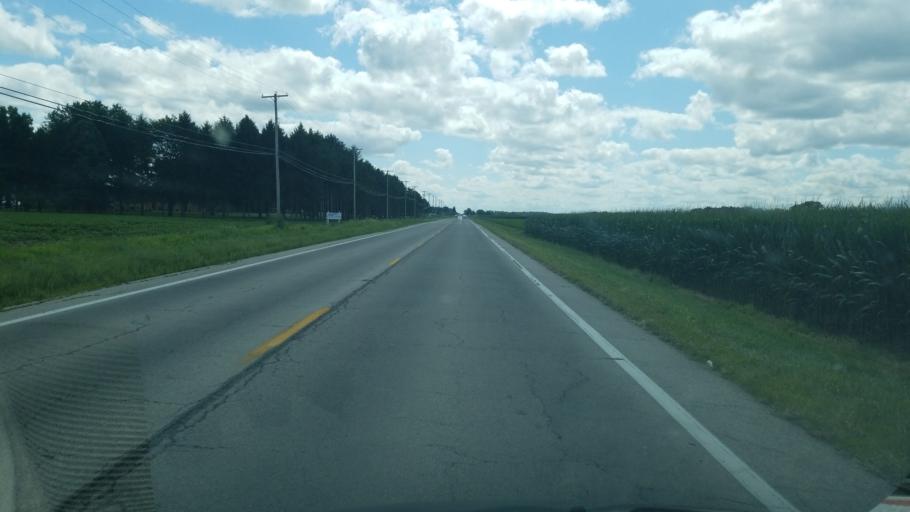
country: US
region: Ohio
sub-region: Henry County
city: Napoleon
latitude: 41.3605
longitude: -84.1200
